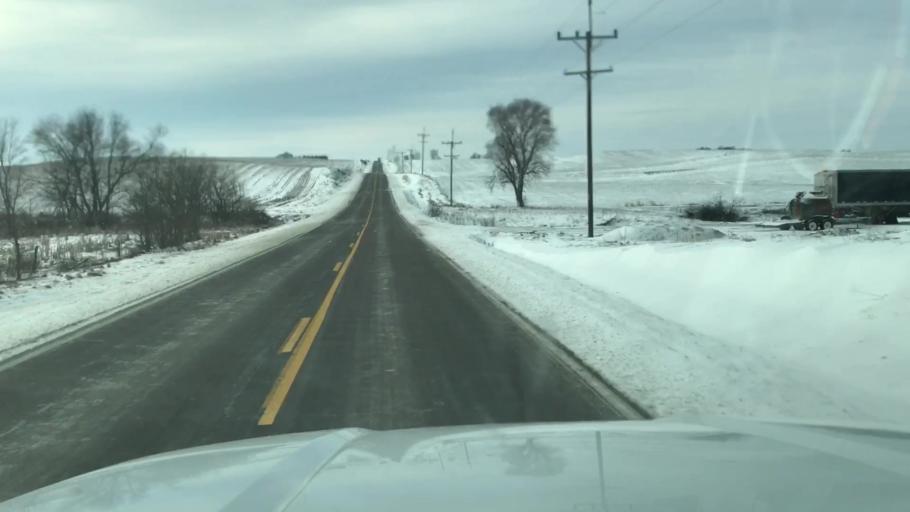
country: US
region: Missouri
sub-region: Holt County
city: Mound City
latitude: 40.1113
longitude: -95.1449
